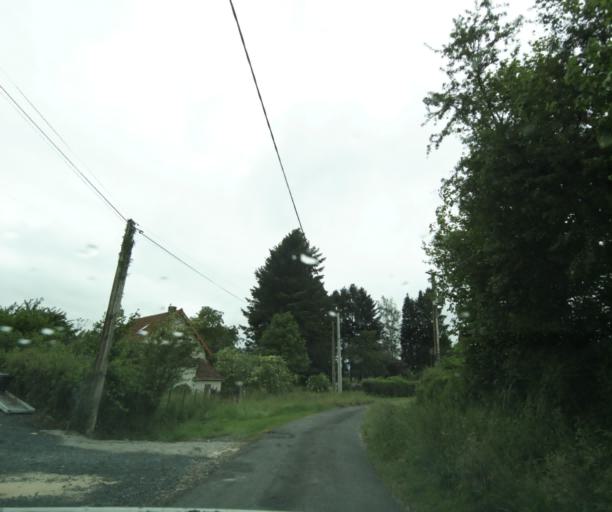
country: FR
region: Bourgogne
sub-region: Departement de Saone-et-Loire
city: Palinges
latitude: 46.4939
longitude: 4.2502
